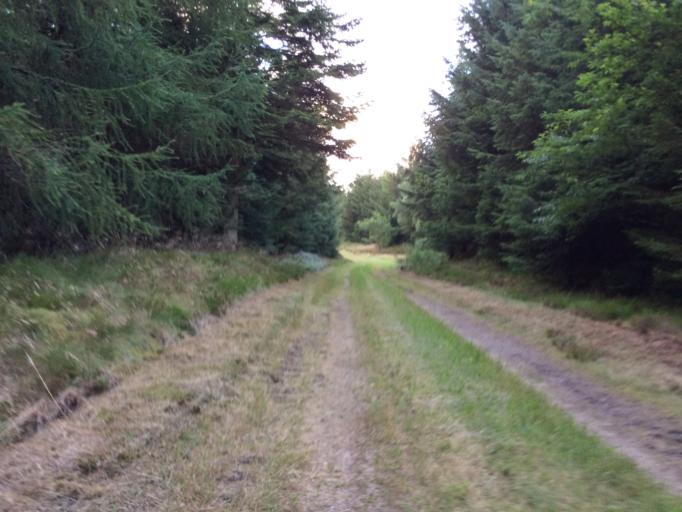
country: DK
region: Central Jutland
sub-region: Holstebro Kommune
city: Ulfborg
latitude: 56.2594
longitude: 8.3775
